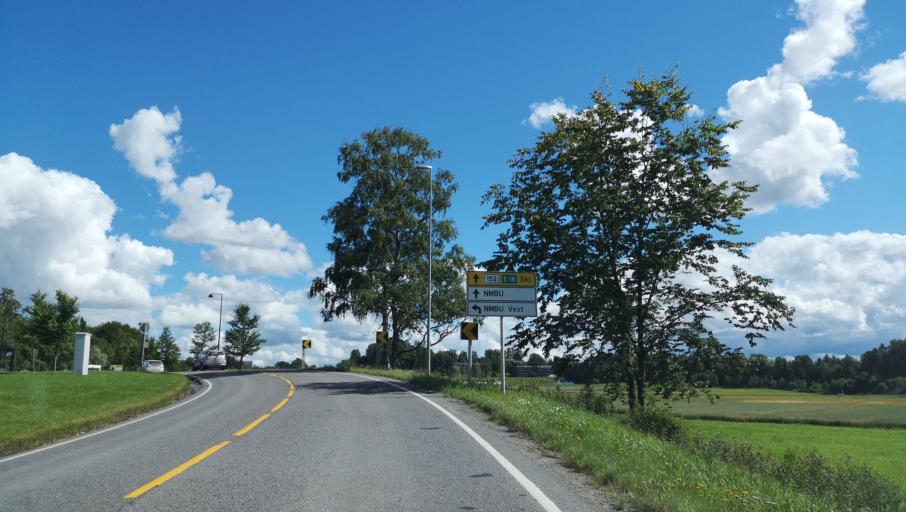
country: NO
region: Akershus
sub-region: As
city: As
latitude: 59.6646
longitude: 10.7580
